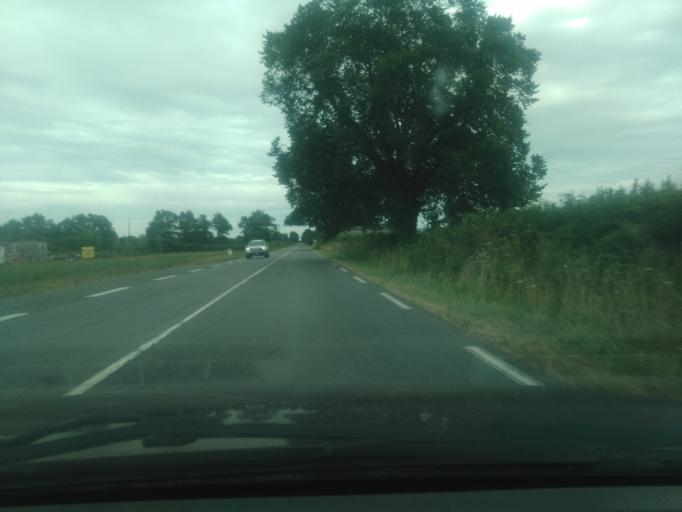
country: FR
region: Centre
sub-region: Departement du Cher
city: Charenton-du-Cher
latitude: 46.7326
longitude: 2.6655
